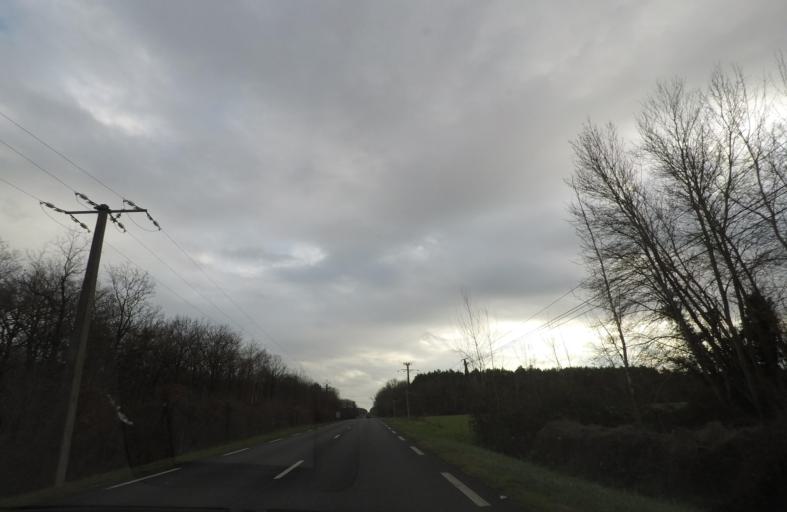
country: FR
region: Centre
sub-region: Departement du Loir-et-Cher
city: Mur-de-Sologne
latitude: 47.4285
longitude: 1.5708
